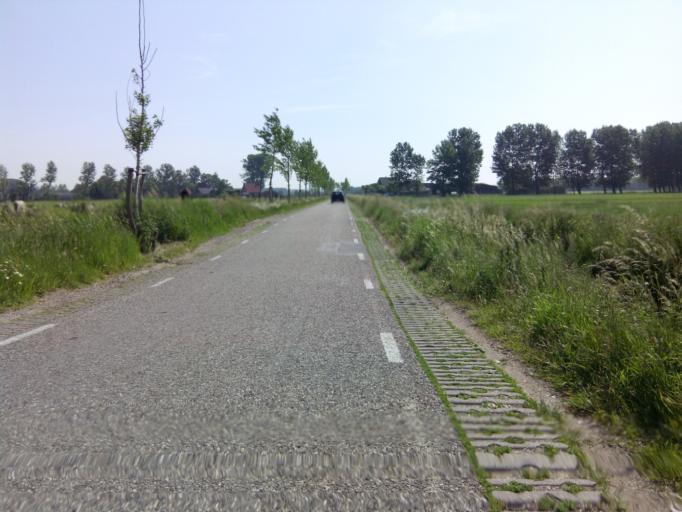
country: NL
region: Utrecht
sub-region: Gemeente Utrechtse Heuvelrug
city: Leersum
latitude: 51.9876
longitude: 5.3947
